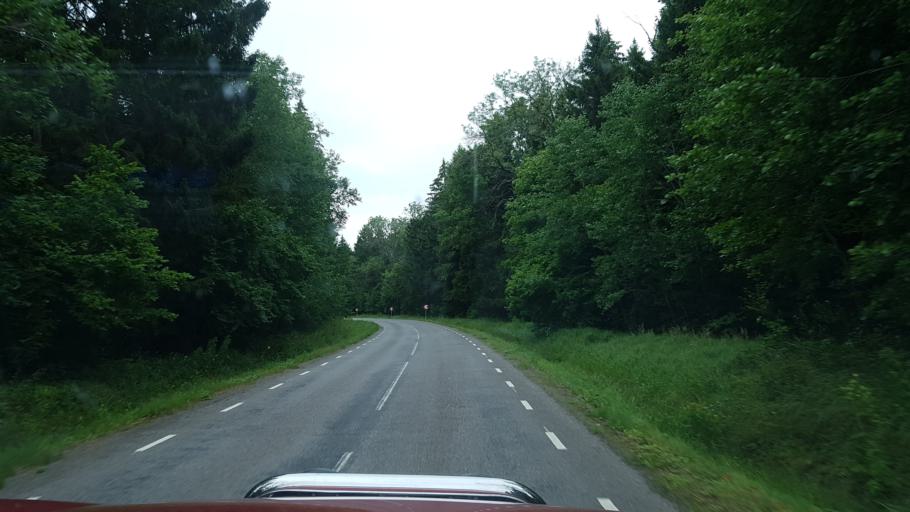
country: EE
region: Ida-Virumaa
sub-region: Johvi vald
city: Johvi
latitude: 59.4321
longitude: 27.3990
